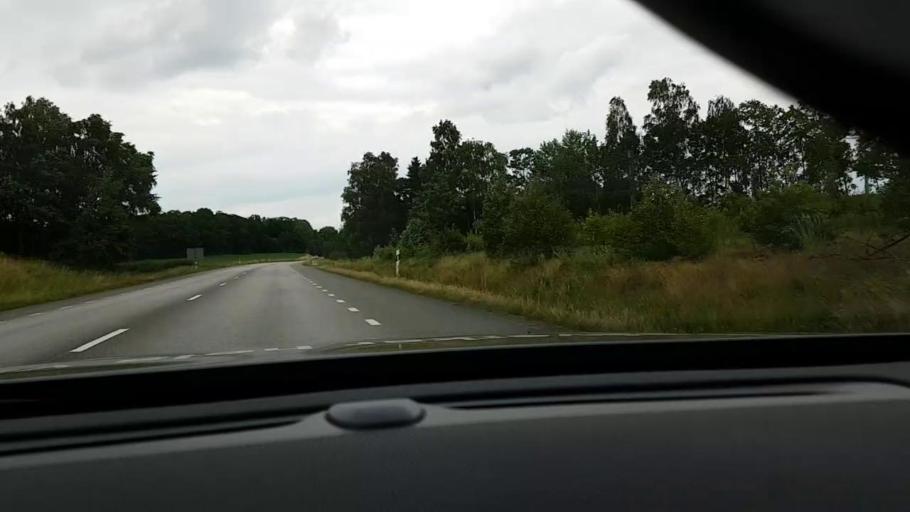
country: SE
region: Skane
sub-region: Hassleholms Kommun
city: Sosdala
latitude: 56.0348
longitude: 13.6892
